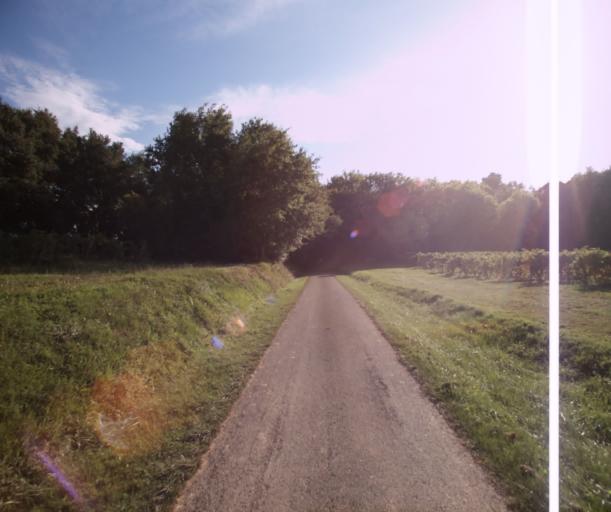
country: FR
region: Midi-Pyrenees
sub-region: Departement du Gers
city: Eauze
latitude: 43.8437
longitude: 0.0341
